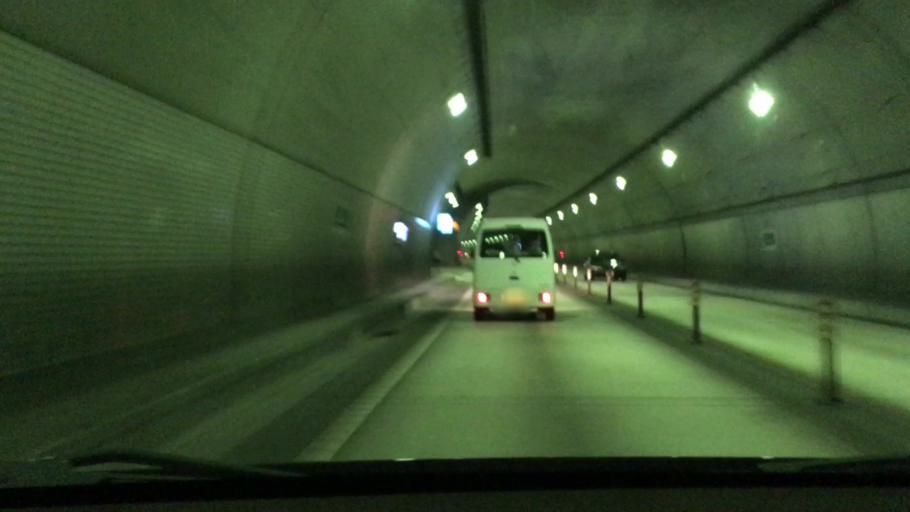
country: JP
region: Nagasaki
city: Sasebo
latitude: 33.0969
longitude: 129.7791
